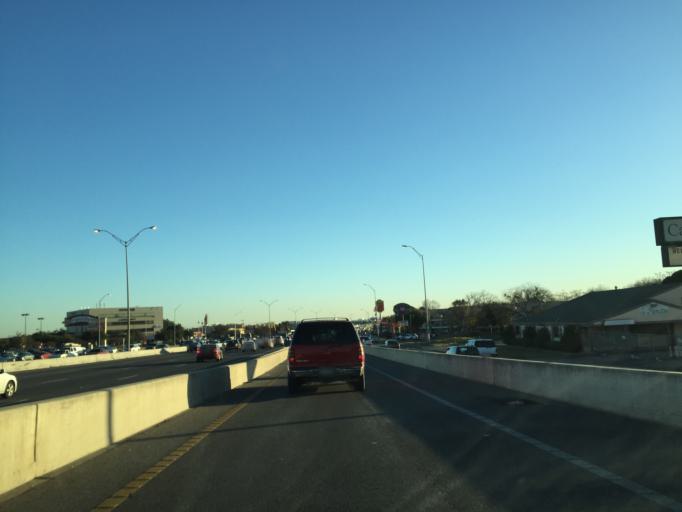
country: US
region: Texas
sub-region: Travis County
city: Austin
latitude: 30.3175
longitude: -97.7077
